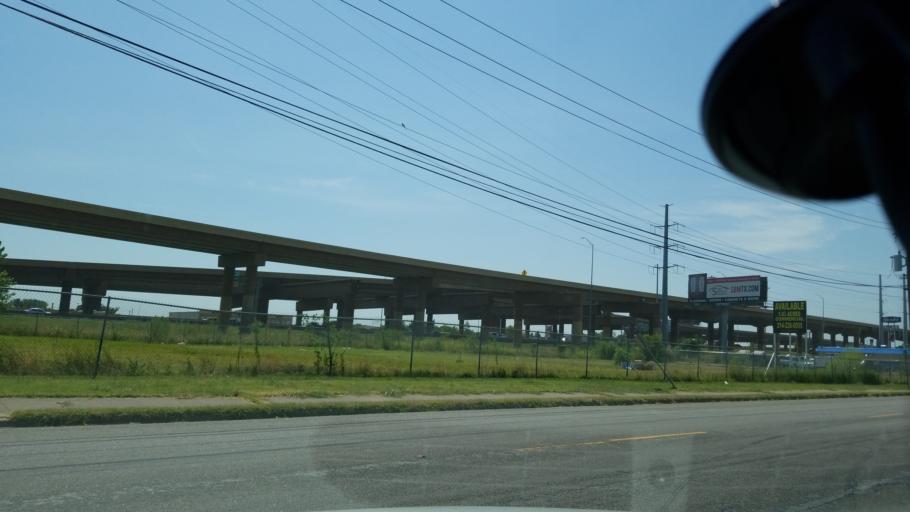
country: US
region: Texas
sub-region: Dallas County
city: Farmers Branch
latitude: 32.9034
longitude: -96.8996
